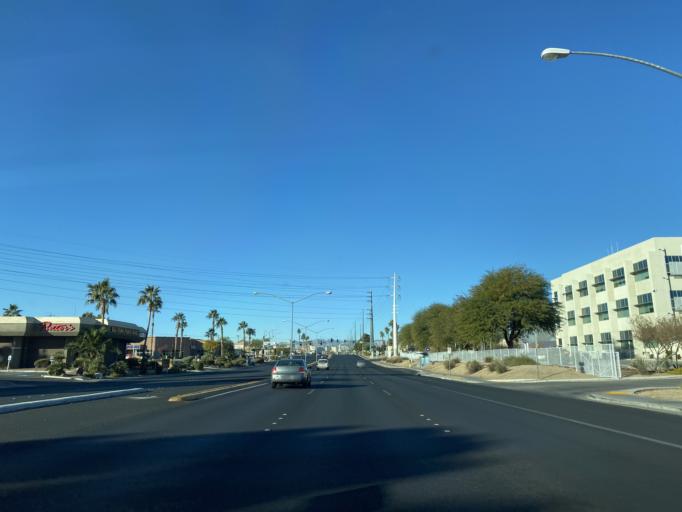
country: US
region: Nevada
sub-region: Clark County
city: Winchester
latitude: 36.1151
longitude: -115.1074
